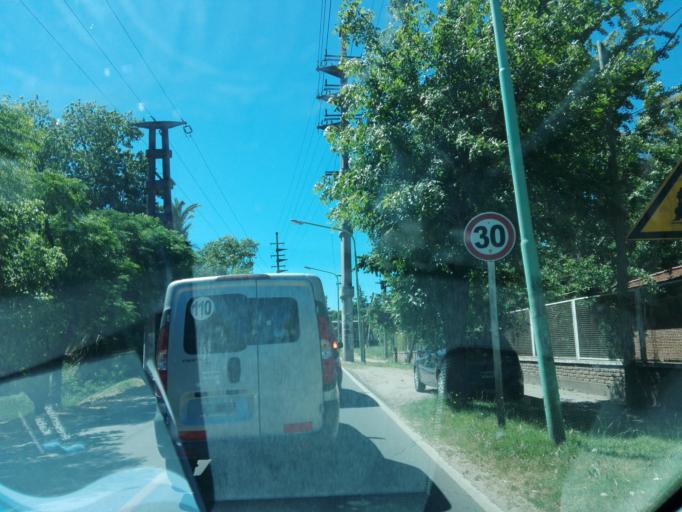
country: AR
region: Buenos Aires
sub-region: Partido de La Plata
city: La Plata
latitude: -34.8981
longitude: -57.9270
